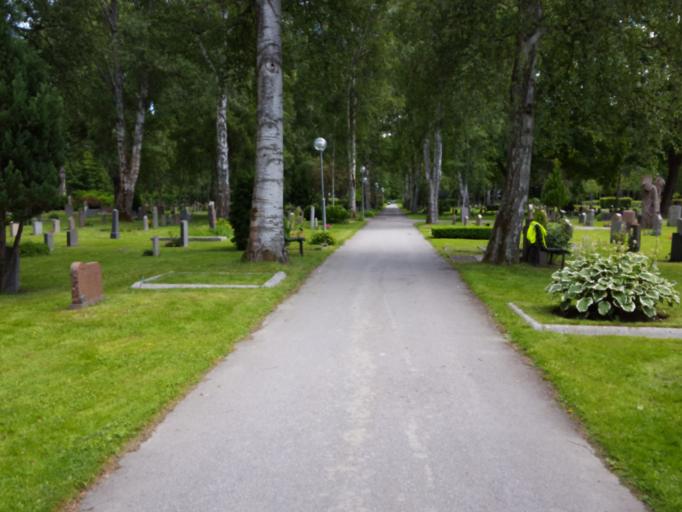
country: SE
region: Stockholm
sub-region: Solna Kommun
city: Solna
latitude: 59.3530
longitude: 18.0258
